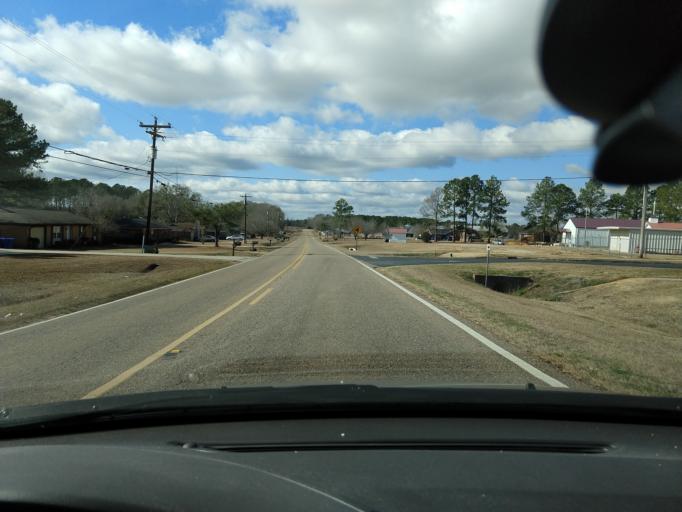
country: US
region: Alabama
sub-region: Coffee County
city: Enterprise
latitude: 31.3230
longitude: -85.9011
